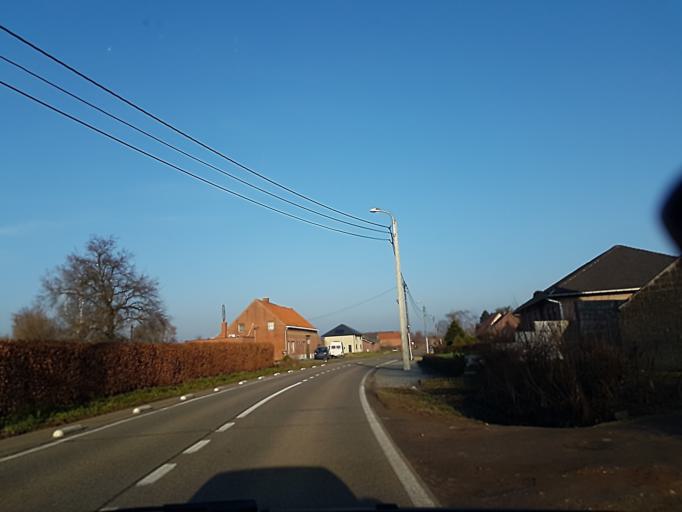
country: BE
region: Flanders
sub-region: Provincie Antwerpen
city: Heist-op-den-Berg
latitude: 51.0358
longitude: 4.7117
